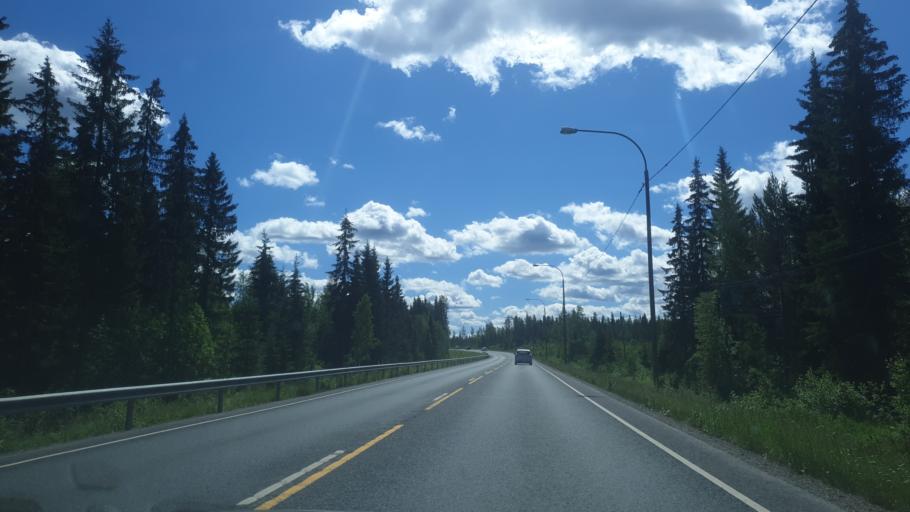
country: FI
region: Northern Savo
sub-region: Varkaus
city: Leppaevirta
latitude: 62.5718
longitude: 27.6093
